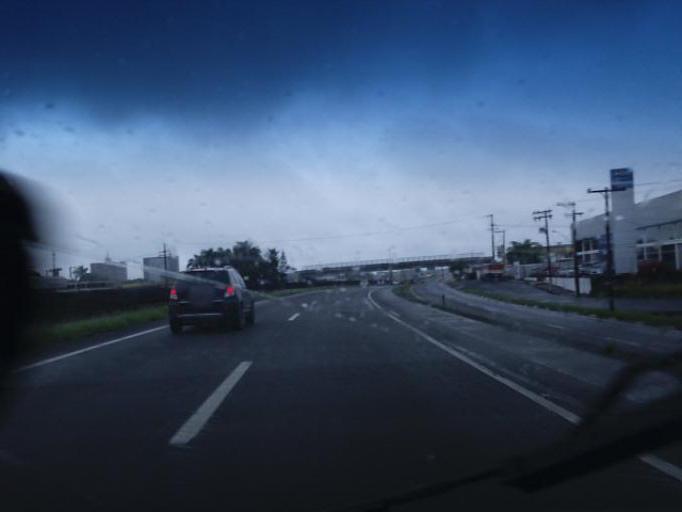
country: BR
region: Sao Paulo
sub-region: Registro
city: Registro
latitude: -24.5024
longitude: -47.8467
